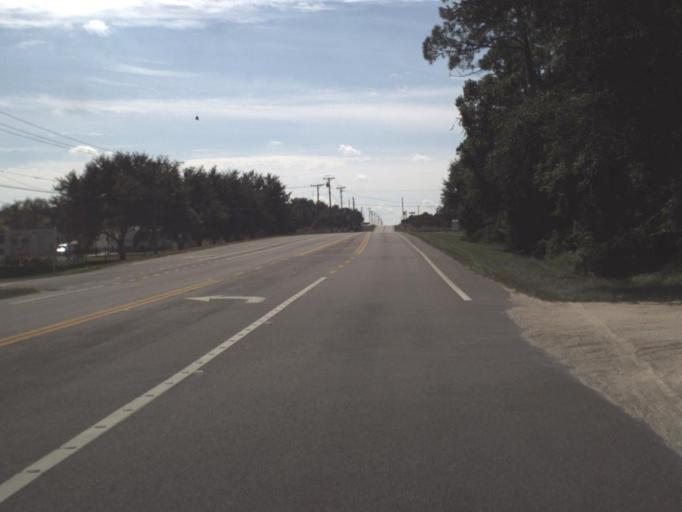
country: US
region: Florida
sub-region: Highlands County
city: Sebring
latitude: 27.5433
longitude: -81.4534
